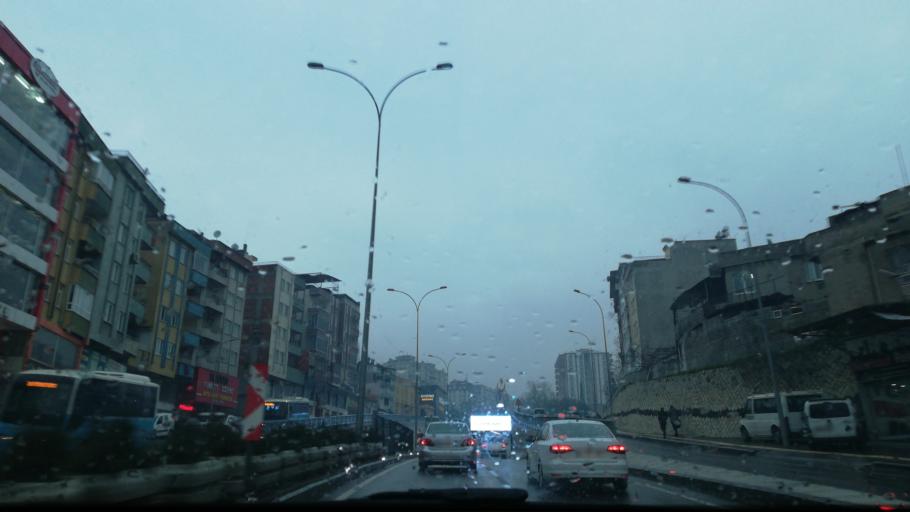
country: TR
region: Kahramanmaras
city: Kahramanmaras
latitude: 37.5848
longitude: 36.9190
